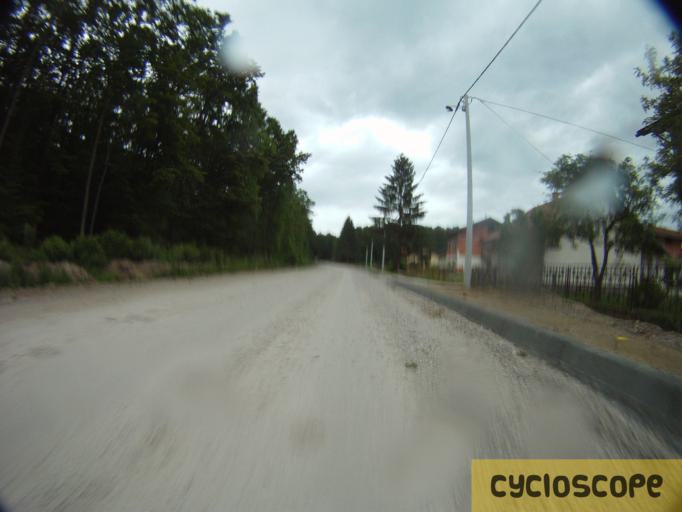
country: HR
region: Karlovacka
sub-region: Grad Karlovac
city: Karlovac
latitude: 45.5271
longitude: 15.5916
